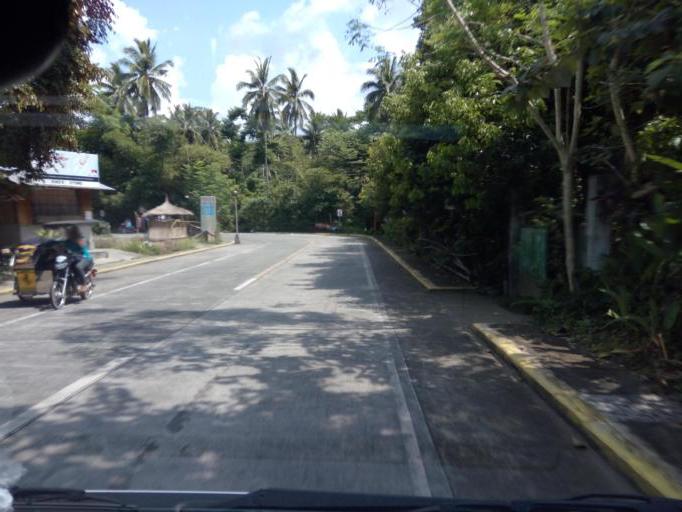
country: PH
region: Central Luzon
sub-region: Province of Aurora
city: Maria Aurora
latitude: 15.8005
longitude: 121.4746
